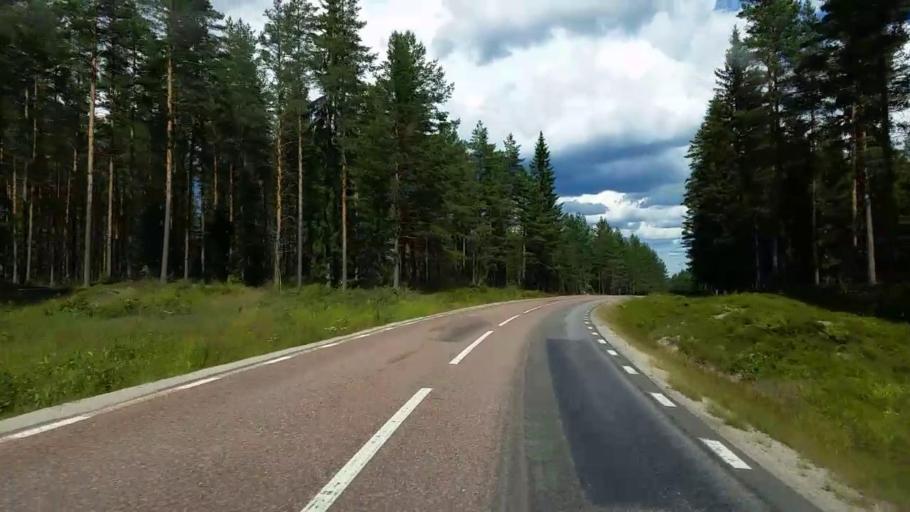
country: SE
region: Gaevleborg
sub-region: Ovanakers Kommun
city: Edsbyn
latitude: 61.3209
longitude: 15.5127
